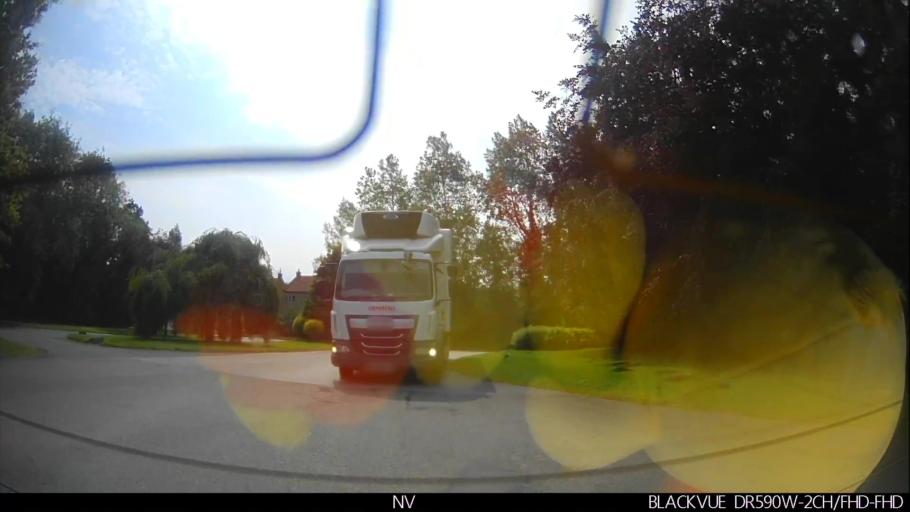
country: GB
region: England
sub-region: North Yorkshire
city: Great Habton
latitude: 54.2058
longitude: -0.8094
